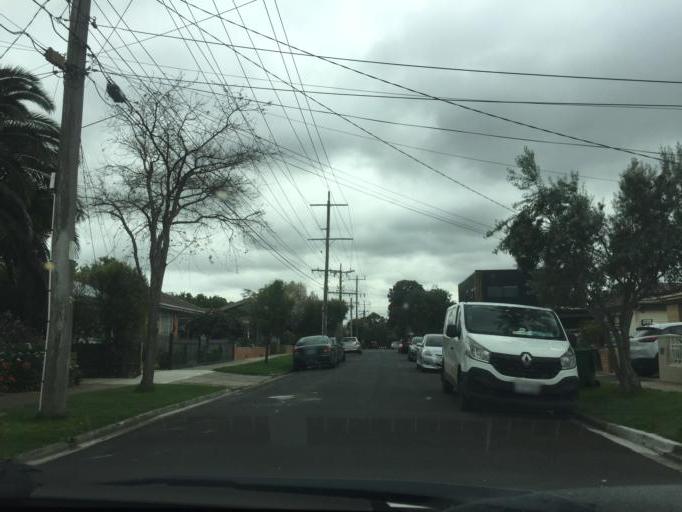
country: AU
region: Victoria
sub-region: Maribyrnong
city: Kingsville
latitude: -37.8170
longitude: 144.8721
